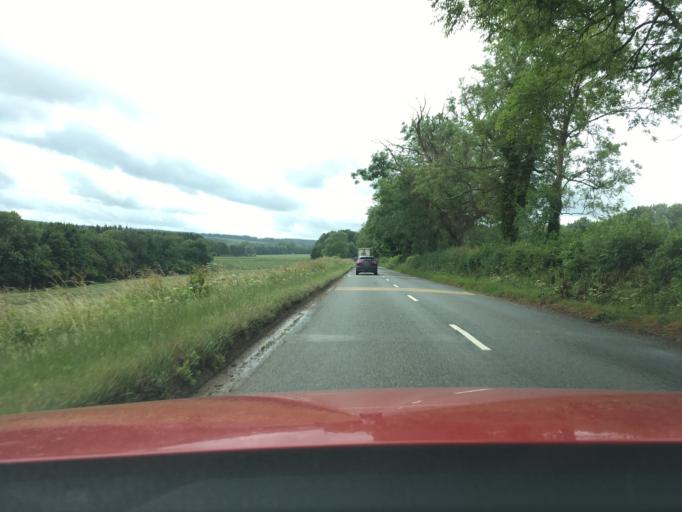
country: GB
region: England
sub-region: Gloucestershire
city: Chipping Campden
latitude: 52.0511
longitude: -1.8017
